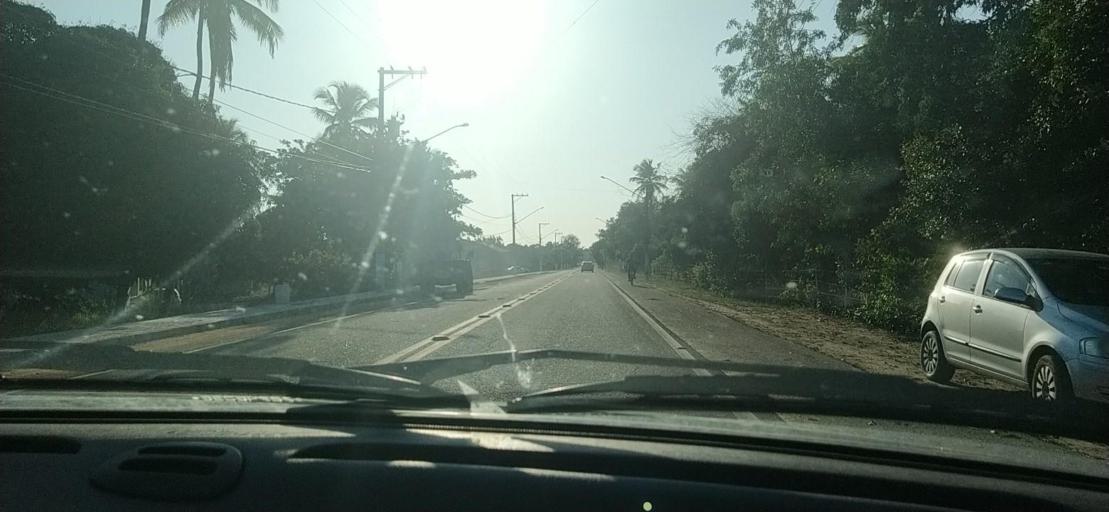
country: BR
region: Espirito Santo
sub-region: Conceicao Da Barra
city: Conceicao da Barra
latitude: -18.5677
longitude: -39.7546
